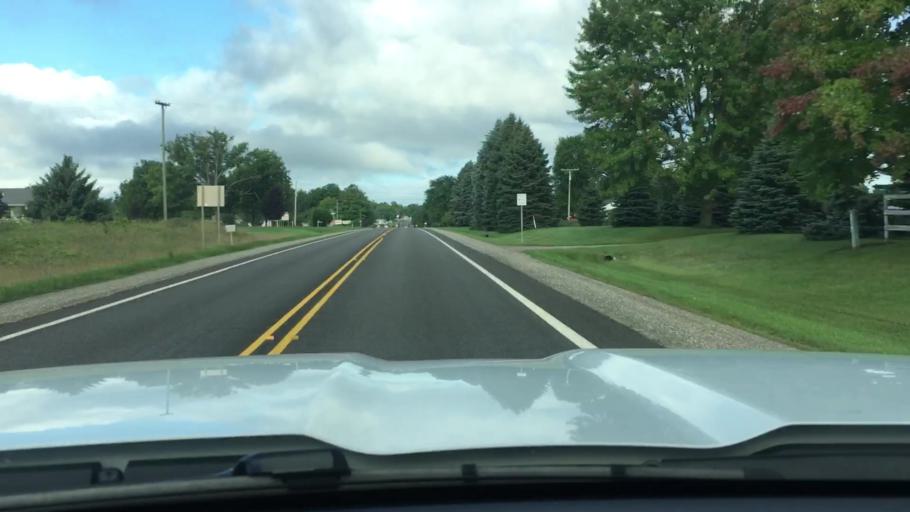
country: US
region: Michigan
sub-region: Lapeer County
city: Barnes Lake-Millers Lake
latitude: 43.3372
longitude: -83.3309
